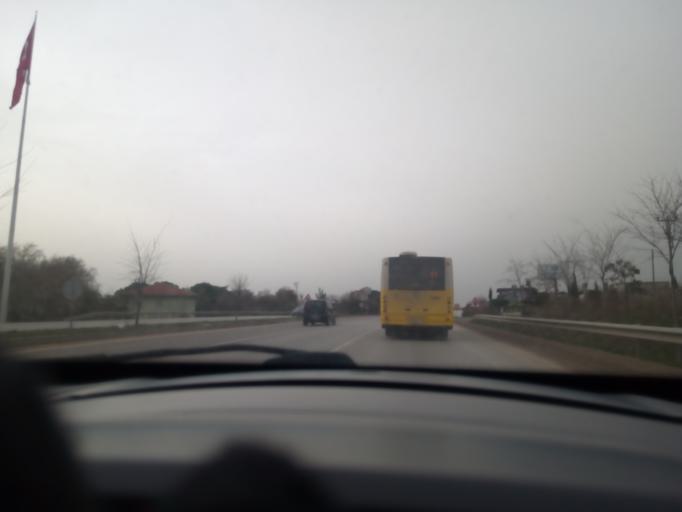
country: TR
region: Balikesir
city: Susurluk
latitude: 39.9485
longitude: 28.1692
